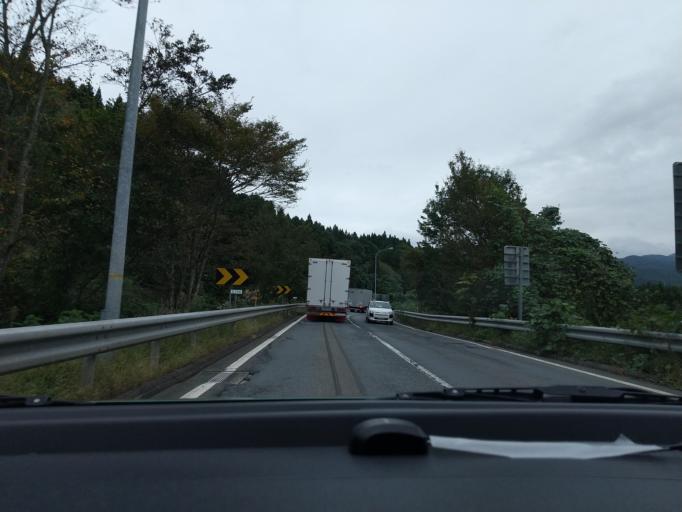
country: JP
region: Iwate
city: Kitakami
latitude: 39.2936
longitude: 140.9824
